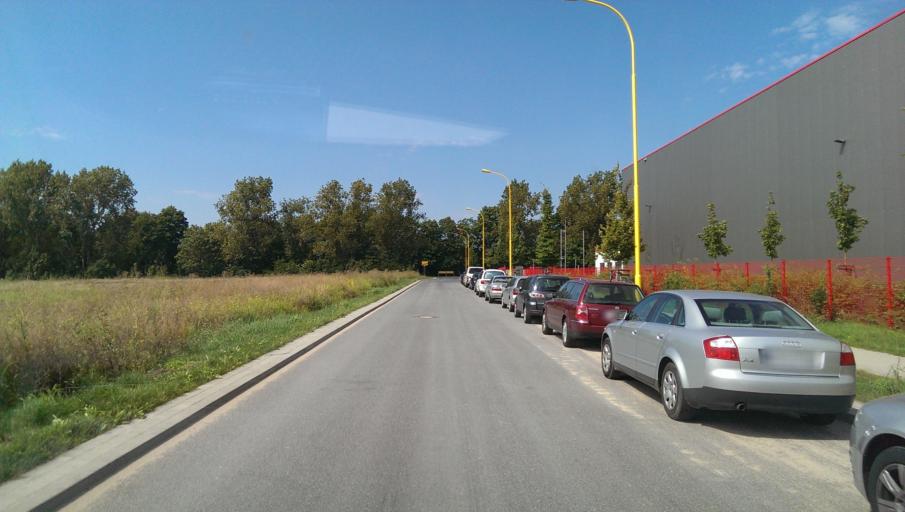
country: DE
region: Brandenburg
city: Grossbeeren
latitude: 52.3765
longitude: 13.3260
